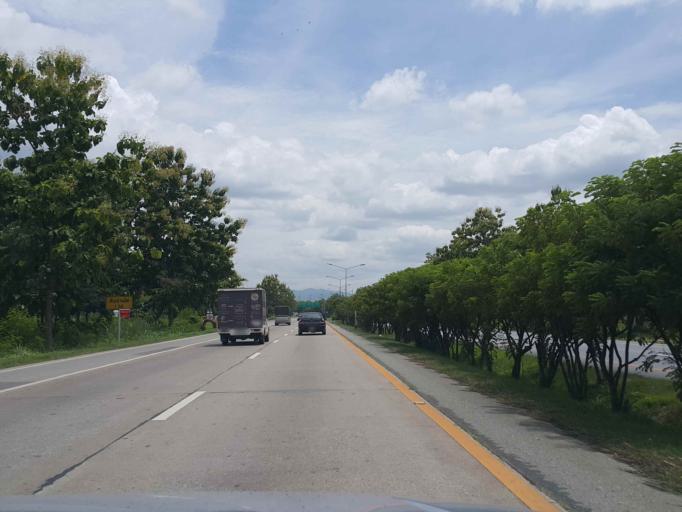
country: TH
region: Lamphun
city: Lamphun
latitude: 18.5617
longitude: 99.0455
